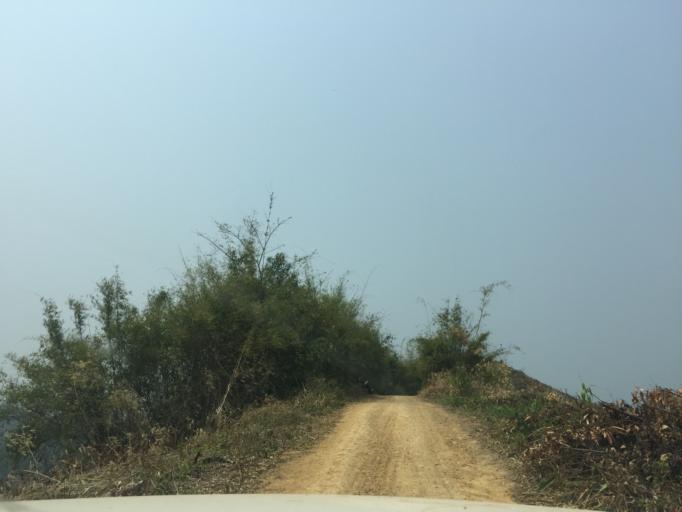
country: LA
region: Loungnamtha
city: Muang Nale
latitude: 20.6299
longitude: 101.6373
